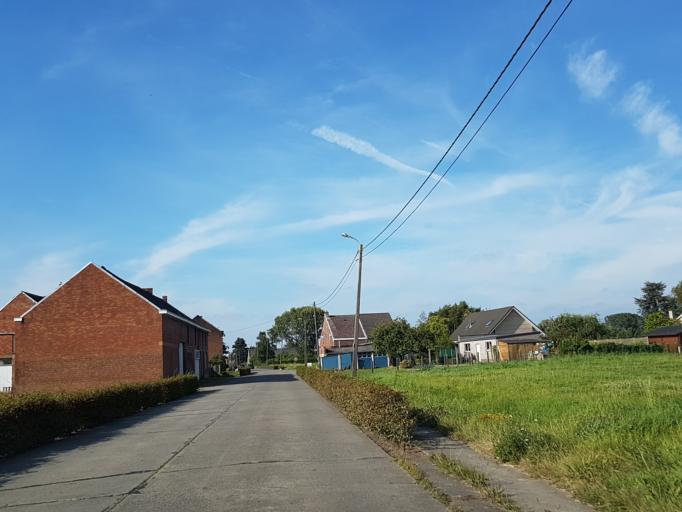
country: BE
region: Flanders
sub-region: Provincie Vlaams-Brabant
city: Zemst
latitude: 51.0016
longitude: 4.4254
